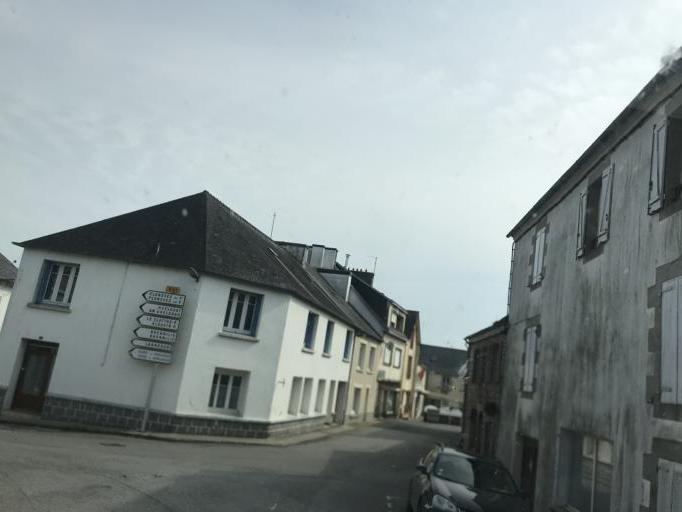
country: FR
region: Brittany
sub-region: Departement du Finistere
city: Brasparts
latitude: 48.3021
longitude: -3.9558
